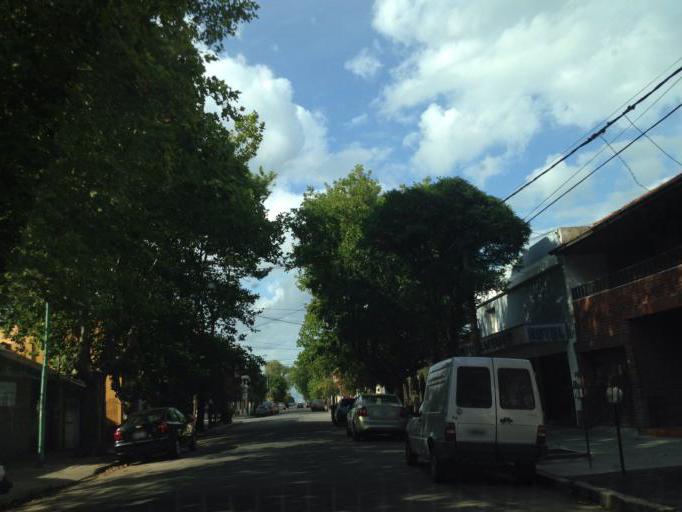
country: AR
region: Buenos Aires
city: Mar del Plata
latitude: -37.9870
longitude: -57.5483
